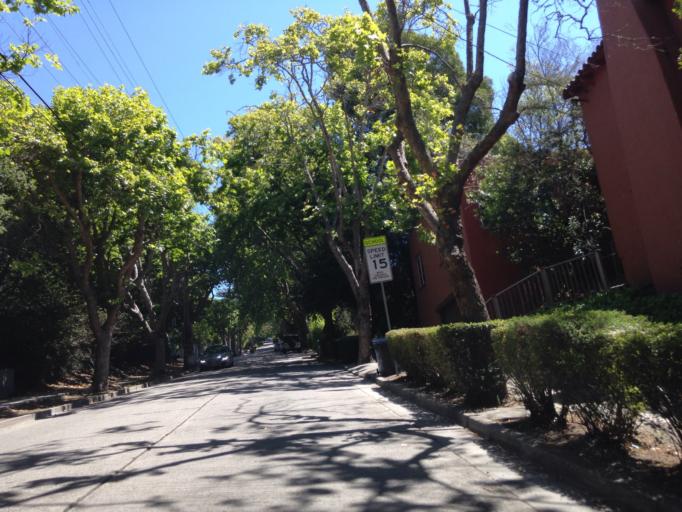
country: US
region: California
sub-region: Contra Costa County
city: Kensington
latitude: 37.8932
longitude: -122.2677
